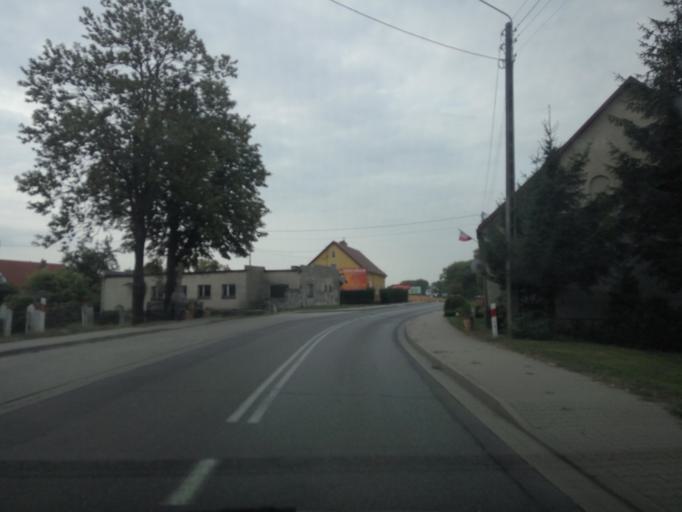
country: PL
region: Lower Silesian Voivodeship
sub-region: Powiat wroclawski
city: Zorawina
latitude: 50.8939
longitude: 17.0636
